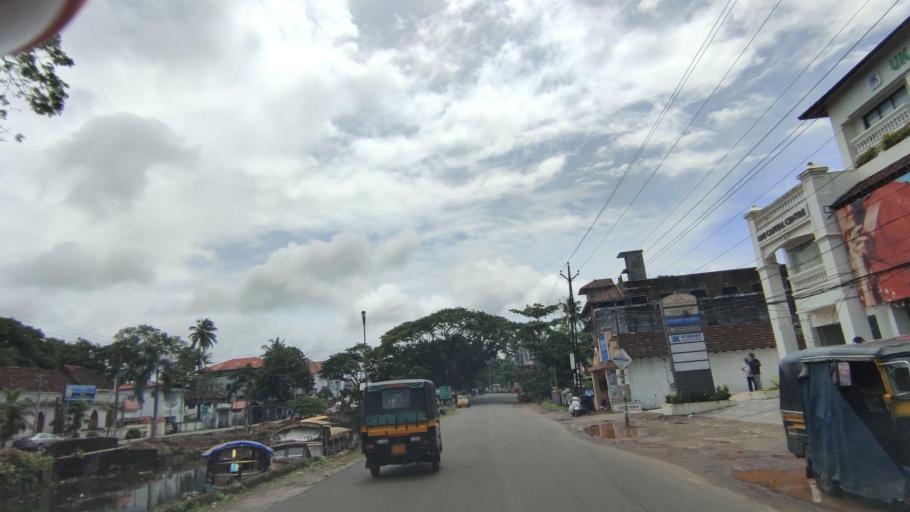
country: IN
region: Kerala
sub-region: Alappuzha
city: Alleppey
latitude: 9.5004
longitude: 76.3374
